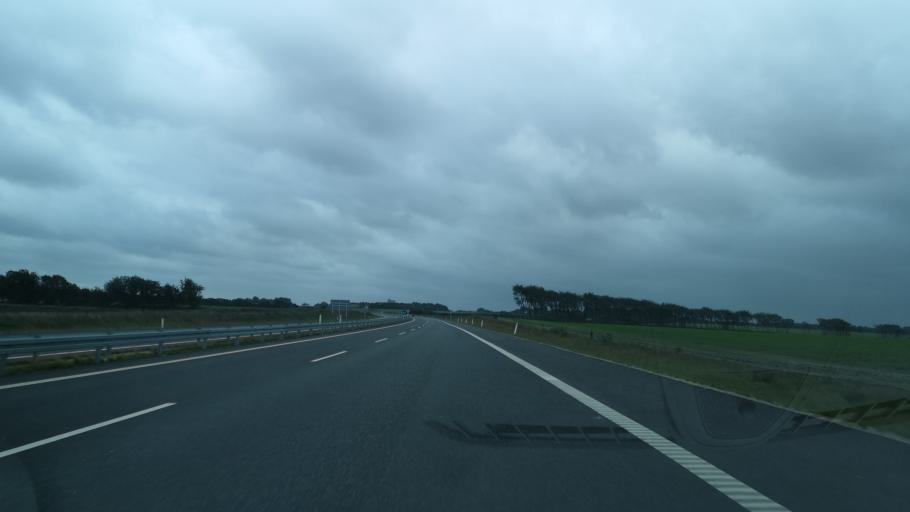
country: DK
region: Central Jutland
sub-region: Herning Kommune
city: Snejbjerg
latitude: 56.1466
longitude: 8.8701
